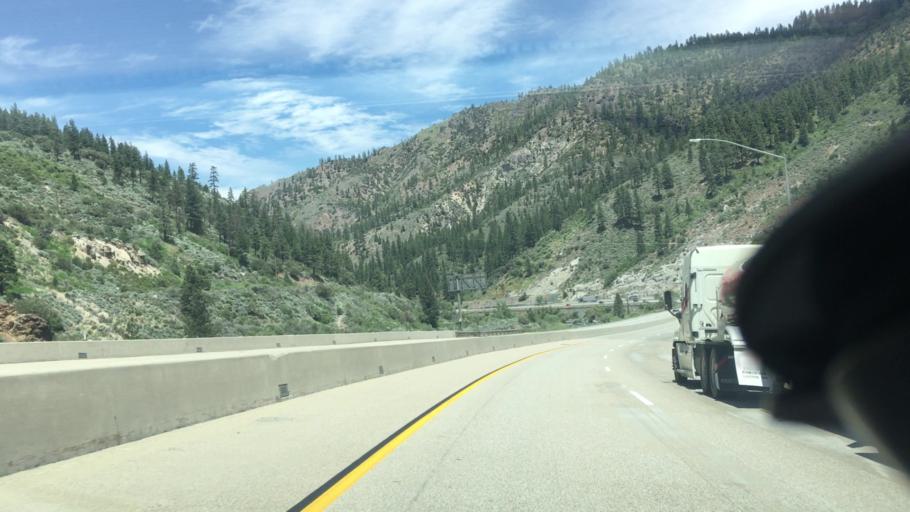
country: US
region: Nevada
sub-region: Washoe County
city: Verdi
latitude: 39.3947
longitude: -120.0252
